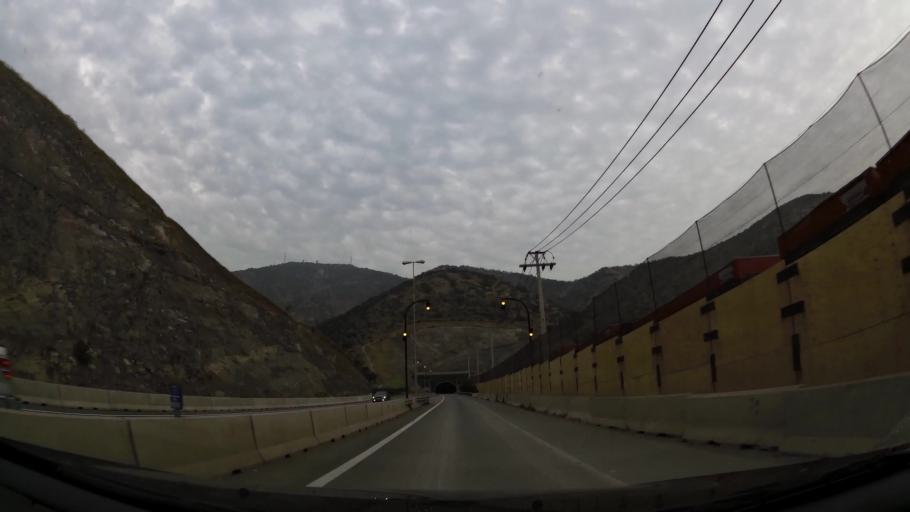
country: CL
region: Santiago Metropolitan
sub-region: Provincia de Chacabuco
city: Chicureo Abajo
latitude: -33.3327
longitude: -70.6276
